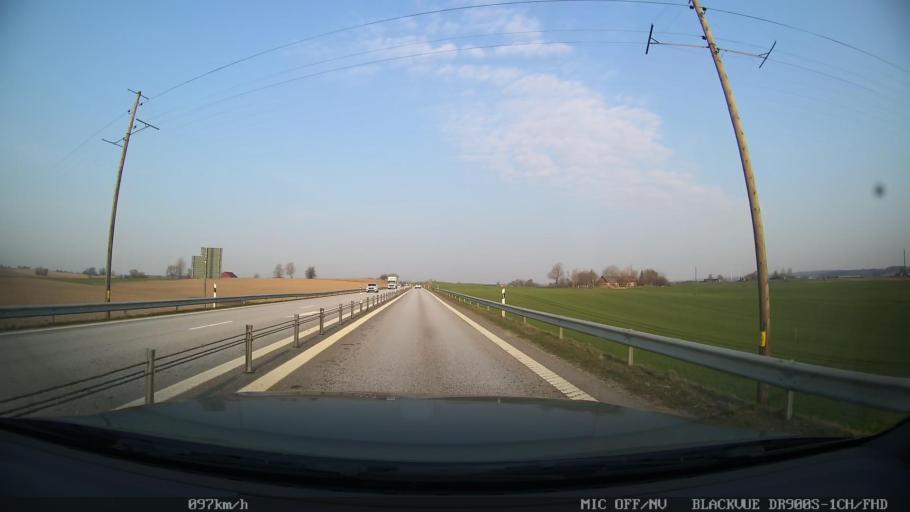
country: SE
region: Skane
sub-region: Skurups Kommun
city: Rydsgard
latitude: 55.4796
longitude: 13.6250
